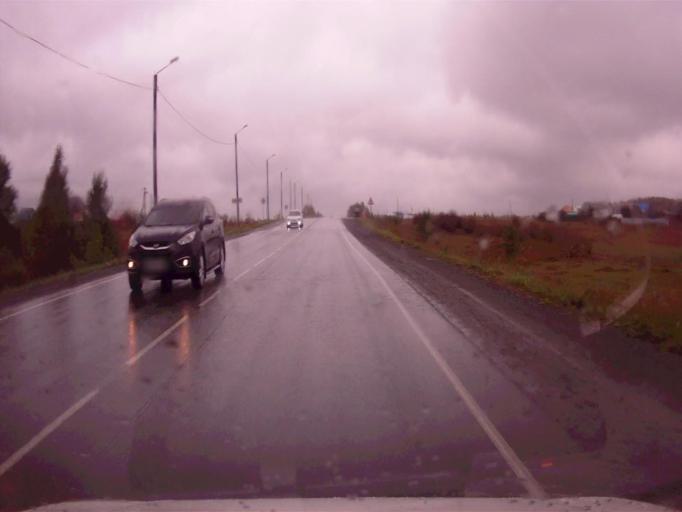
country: RU
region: Chelyabinsk
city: Argayash
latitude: 55.4775
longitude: 60.8593
